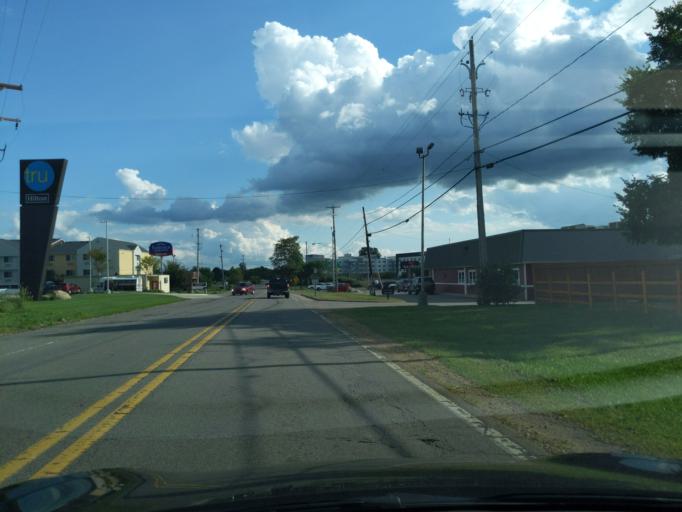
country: US
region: Michigan
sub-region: Jackson County
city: Jackson
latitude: 42.2775
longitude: -84.4295
